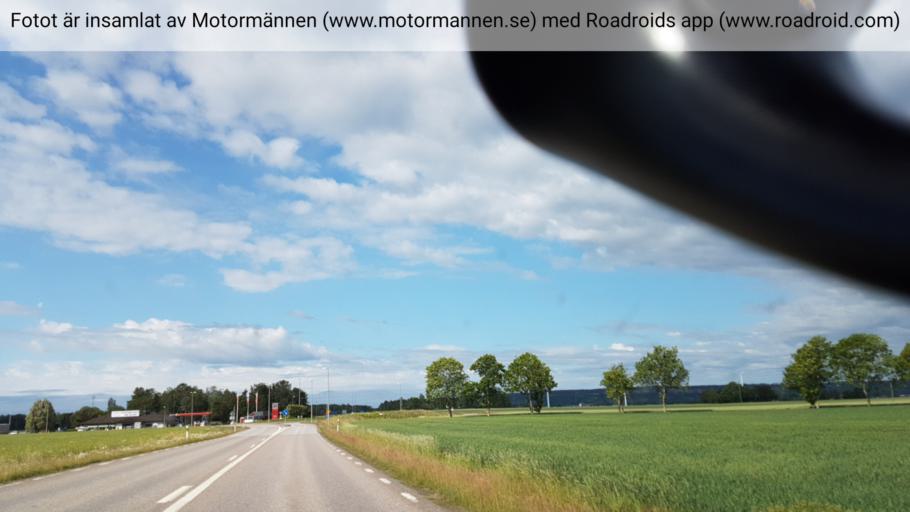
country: SE
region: Vaestra Goetaland
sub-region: Grastorps Kommun
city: Graestorp
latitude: 58.3354
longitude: 12.6140
